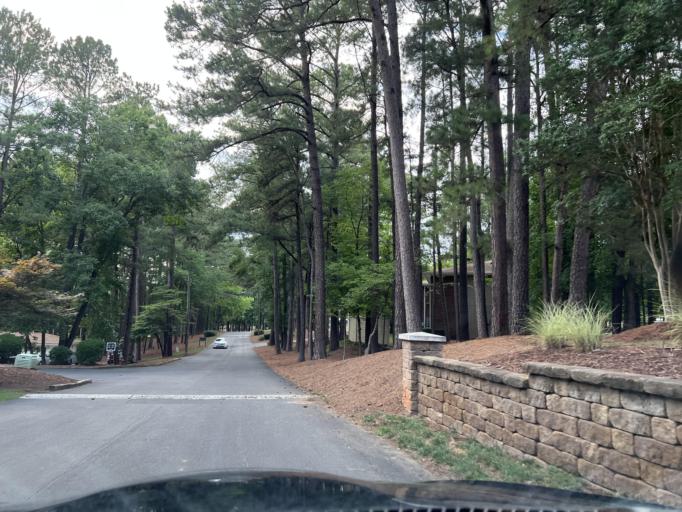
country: US
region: North Carolina
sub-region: Wake County
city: West Raleigh
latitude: 35.8576
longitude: -78.6506
